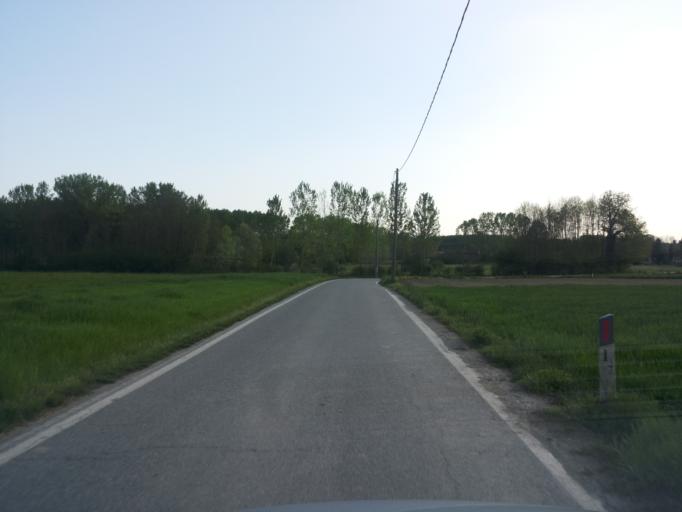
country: IT
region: Piedmont
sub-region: Provincia di Torino
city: Palazzo Canavese
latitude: 45.4441
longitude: 7.9729
